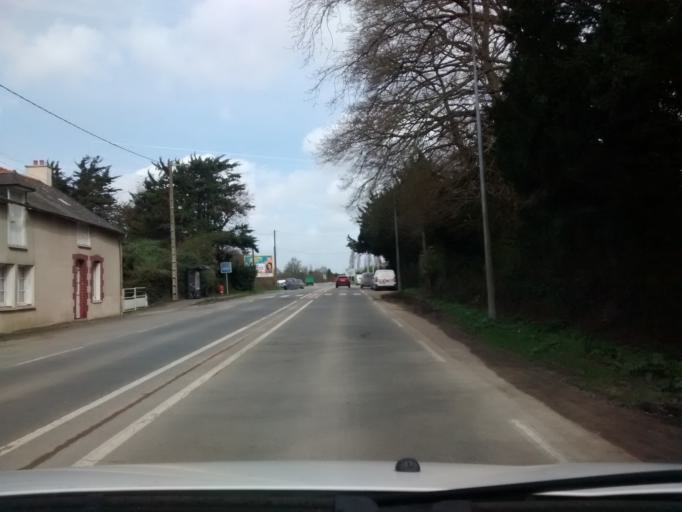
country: FR
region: Brittany
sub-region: Departement d'Ille-et-Vilaine
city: Bruz
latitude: 48.0400
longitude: -1.7553
